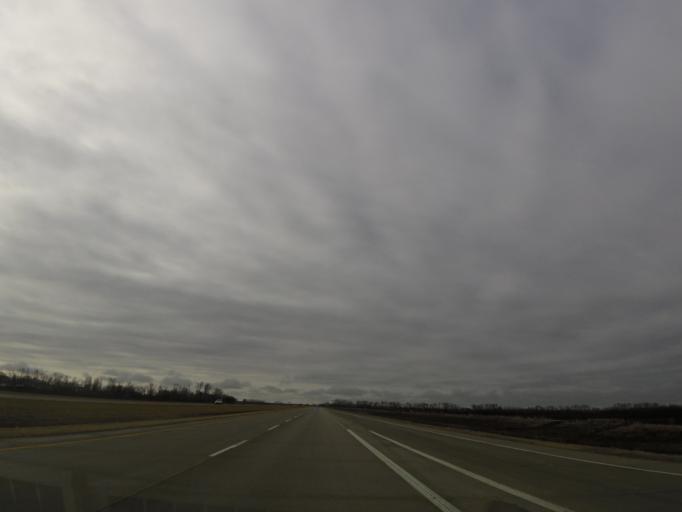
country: US
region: North Dakota
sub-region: Grand Forks County
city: Grand Forks
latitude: 48.1327
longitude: -97.1914
